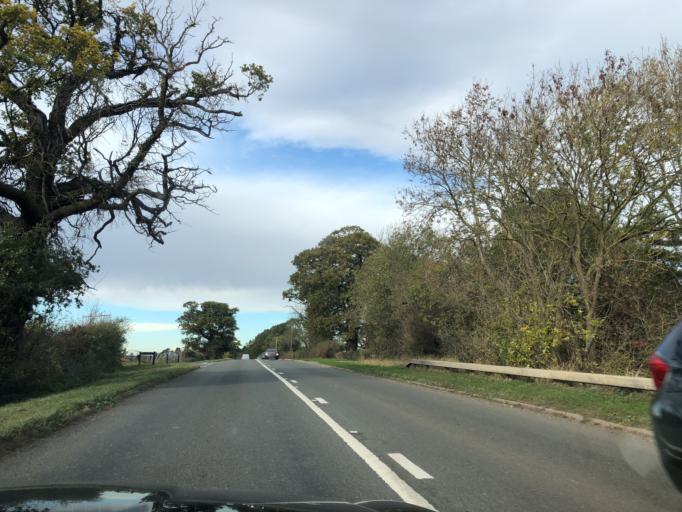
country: GB
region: England
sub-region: Warwickshire
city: Warwick
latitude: 52.2434
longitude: -1.5552
